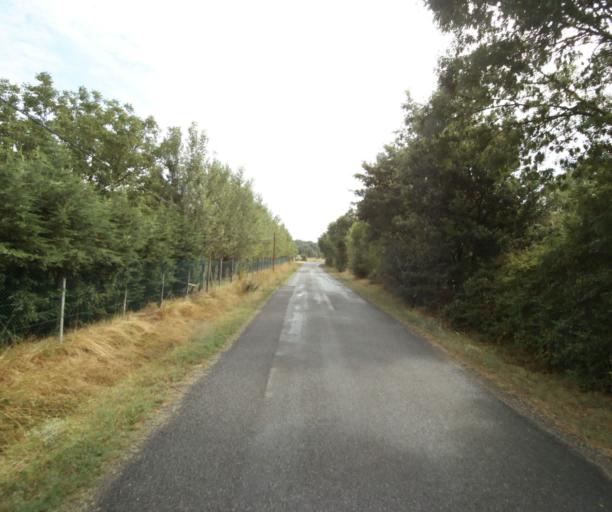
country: FR
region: Midi-Pyrenees
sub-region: Departement de la Haute-Garonne
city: Revel
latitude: 43.4277
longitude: 1.9827
